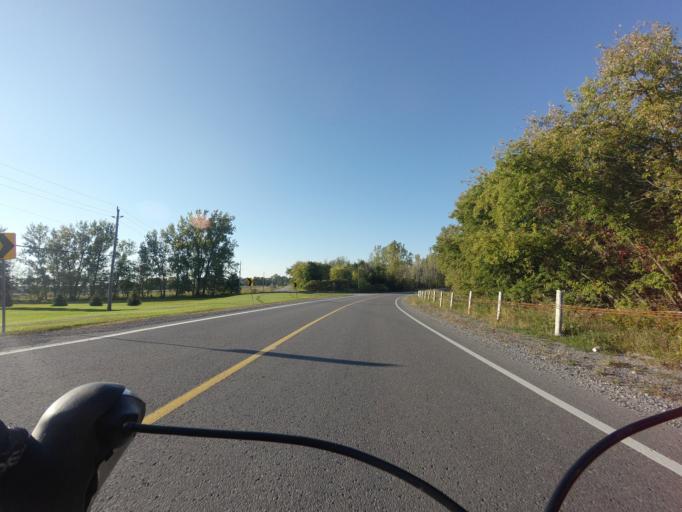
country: CA
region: Ontario
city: Bells Corners
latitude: 45.2145
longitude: -75.7113
